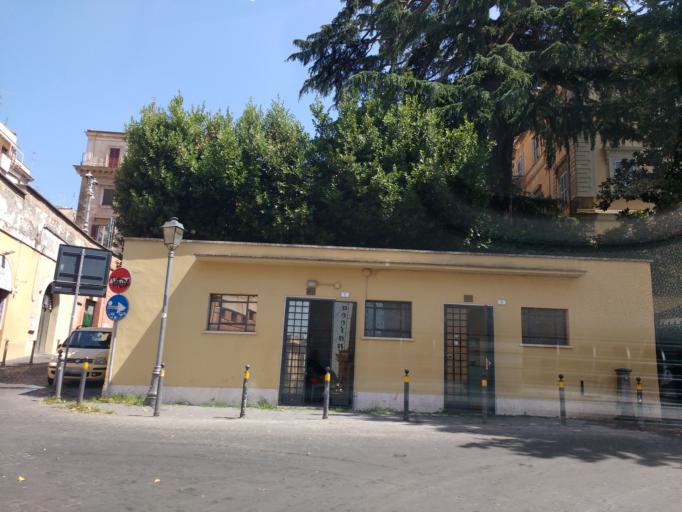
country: IT
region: Latium
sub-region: Citta metropolitana di Roma Capitale
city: Armetta
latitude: 41.8075
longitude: 12.6791
